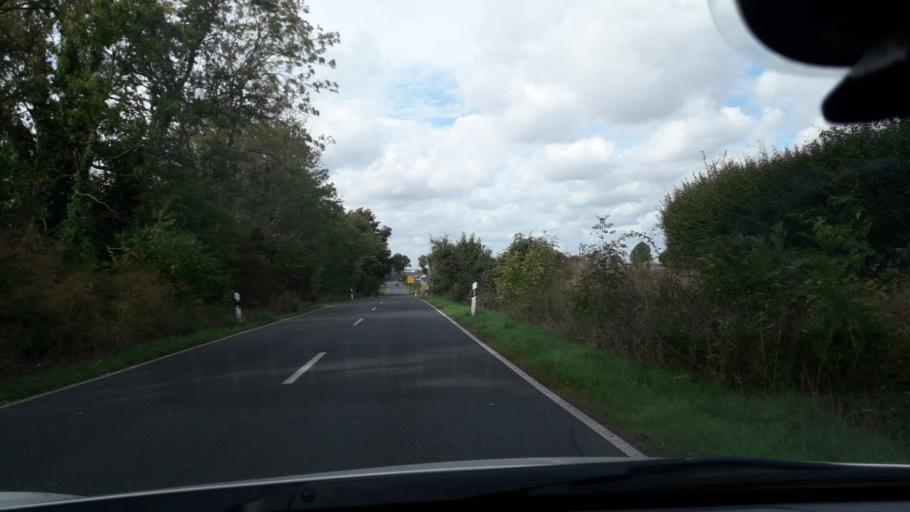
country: DE
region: Lower Saxony
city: Alt Wallmoden
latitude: 52.0251
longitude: 10.3474
